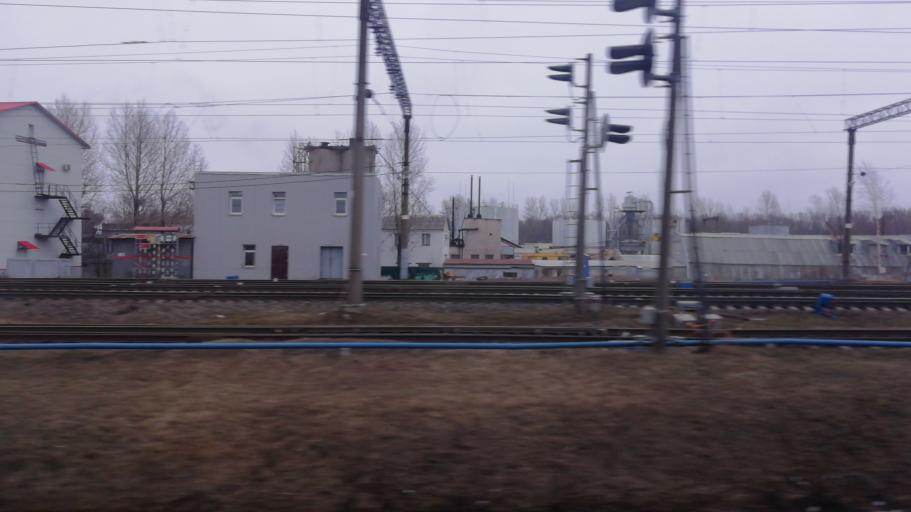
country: RU
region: St.-Petersburg
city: Kupchino
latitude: 59.8824
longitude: 30.3475
